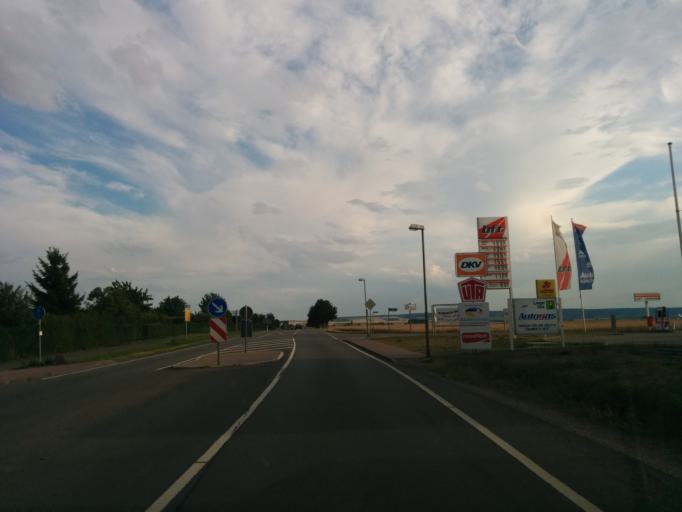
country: DE
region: Thuringia
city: Gebesee
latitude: 51.1104
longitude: 10.9304
